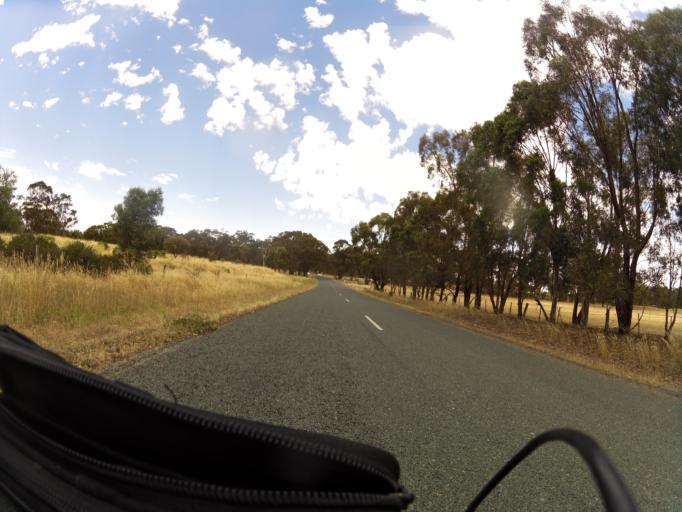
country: AU
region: Victoria
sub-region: Greater Shepparton
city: Shepparton
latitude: -36.6446
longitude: 145.2101
